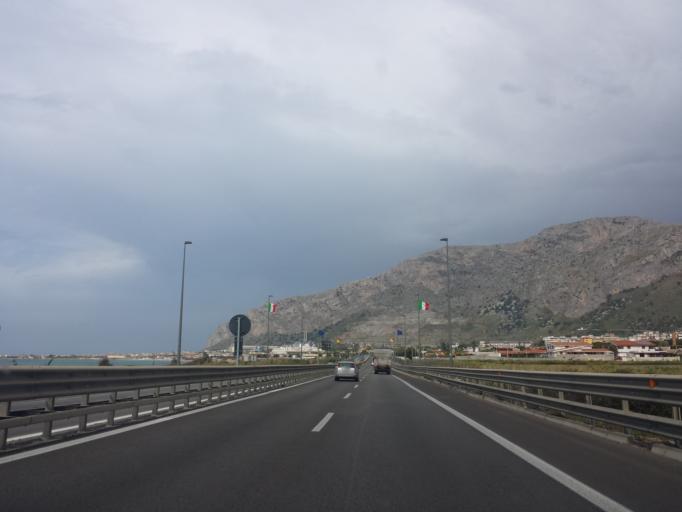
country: IT
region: Sicily
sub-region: Palermo
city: Capaci
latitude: 38.1789
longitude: 13.2267
